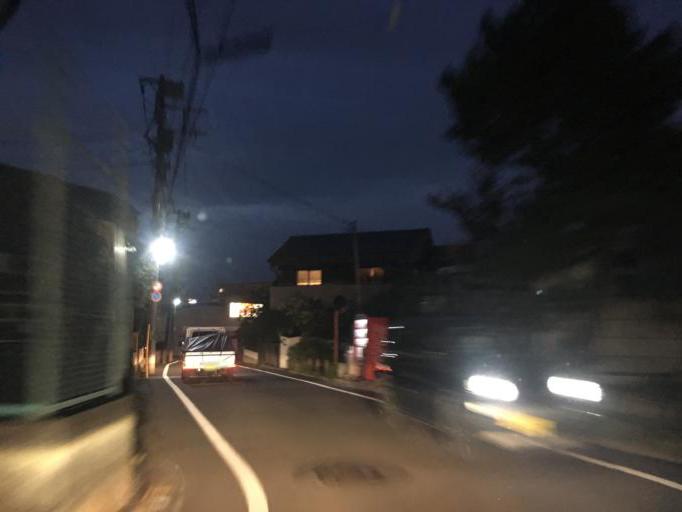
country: JP
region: Tokyo
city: Higashimurayama-shi
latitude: 35.7483
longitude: 139.4504
